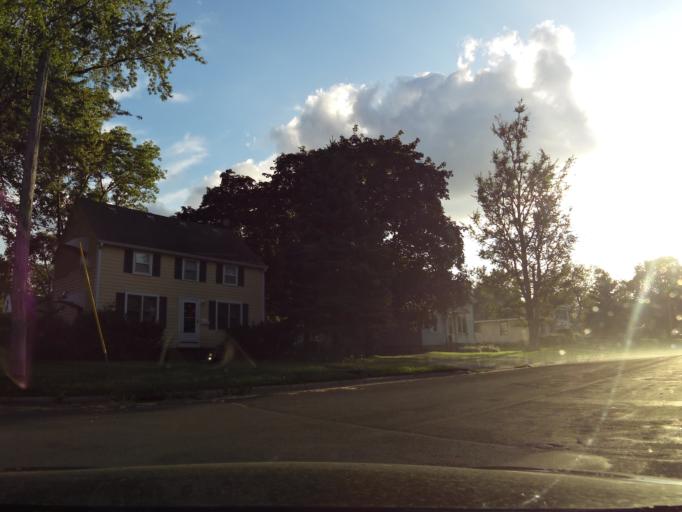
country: US
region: Minnesota
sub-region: Dakota County
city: Hastings
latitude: 44.7343
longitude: -92.8553
